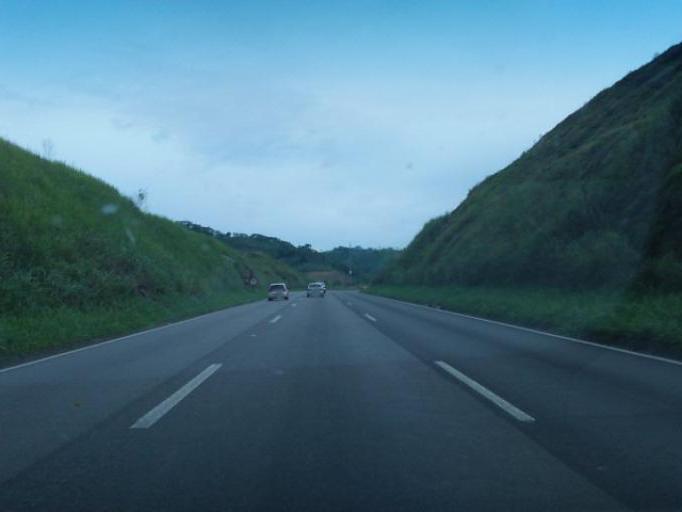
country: BR
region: Sao Paulo
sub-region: Cajati
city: Cajati
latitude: -24.7851
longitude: -48.2082
